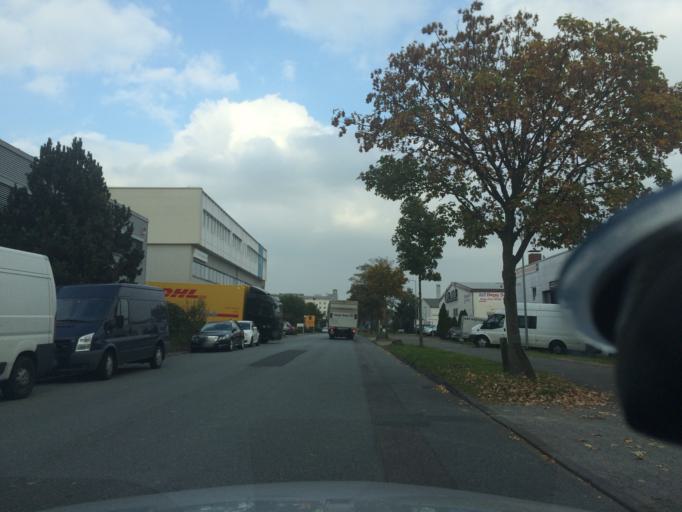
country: DE
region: Hesse
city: Morfelden-Walldorf
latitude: 49.9830
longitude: 8.5810
